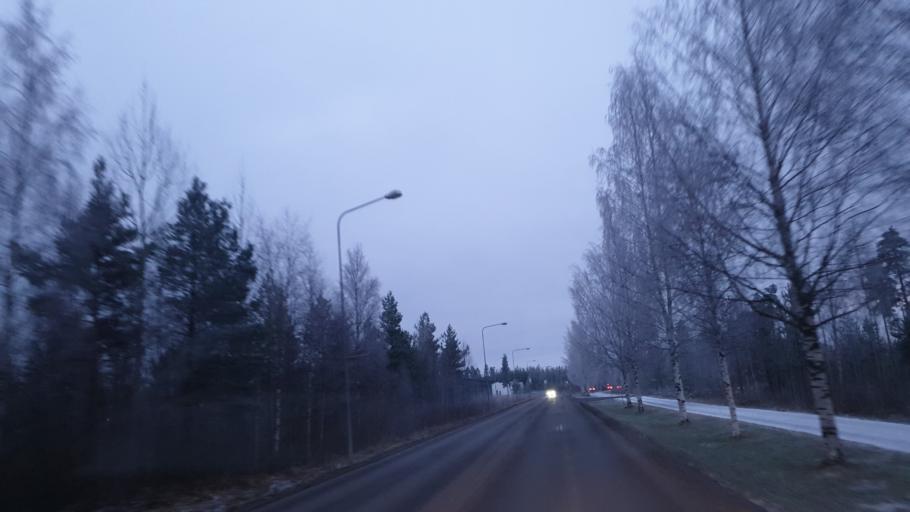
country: FI
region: Southern Ostrobothnia
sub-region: Seinaejoki
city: Nurmo
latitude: 62.7811
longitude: 22.8980
